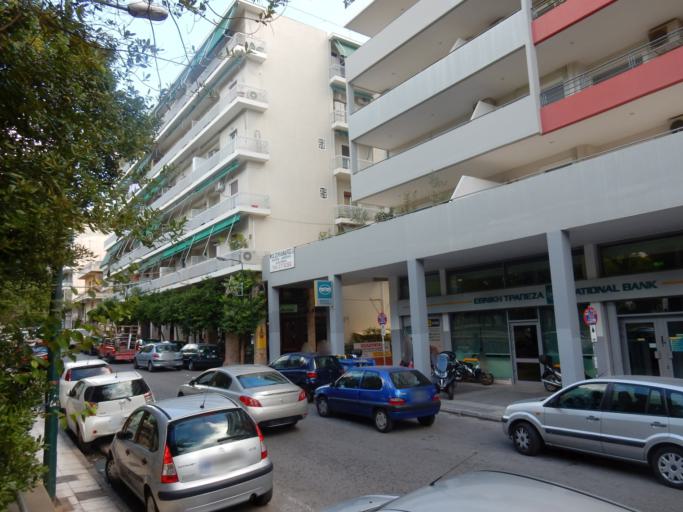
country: GR
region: Attica
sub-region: Nomarchia Athinas
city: Kaisariani
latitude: 37.9816
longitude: 23.7646
